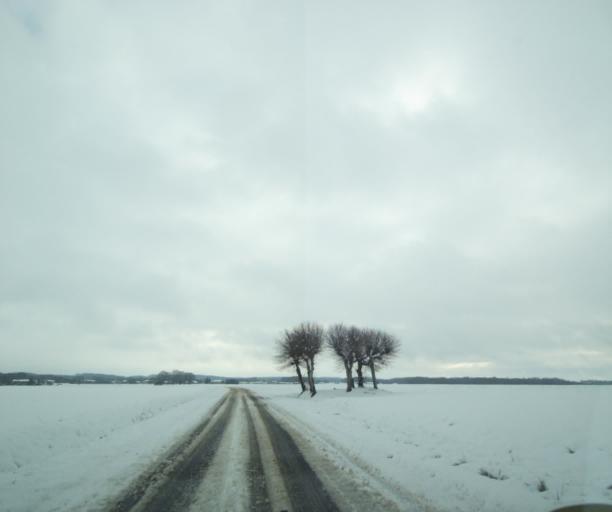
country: FR
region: Champagne-Ardenne
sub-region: Departement de la Haute-Marne
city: Montier-en-Der
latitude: 48.4986
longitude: 4.6878
